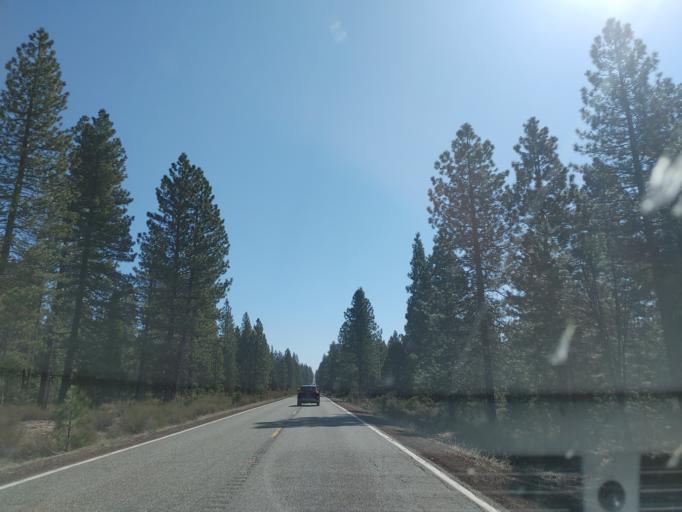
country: US
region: California
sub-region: Siskiyou County
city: McCloud
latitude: 41.2536
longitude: -122.0838
